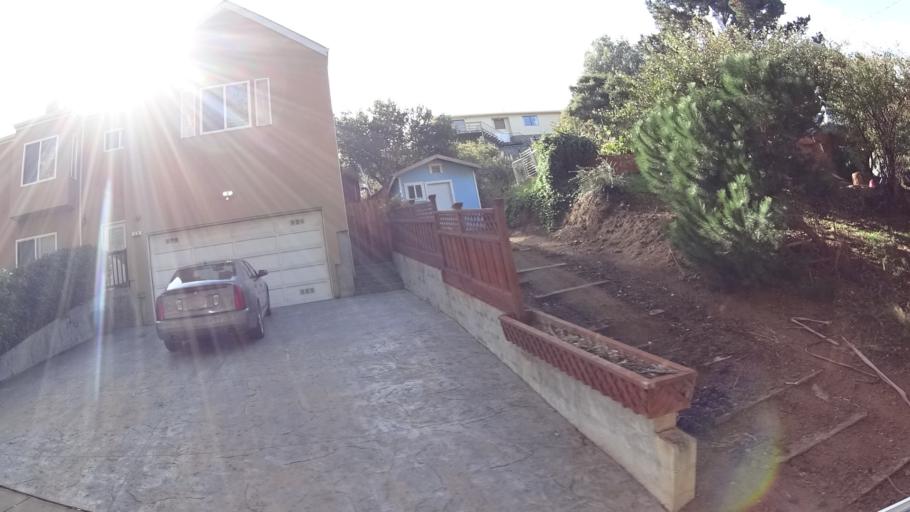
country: US
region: California
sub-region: San Mateo County
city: Brisbane
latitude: 37.6848
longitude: -122.3985
